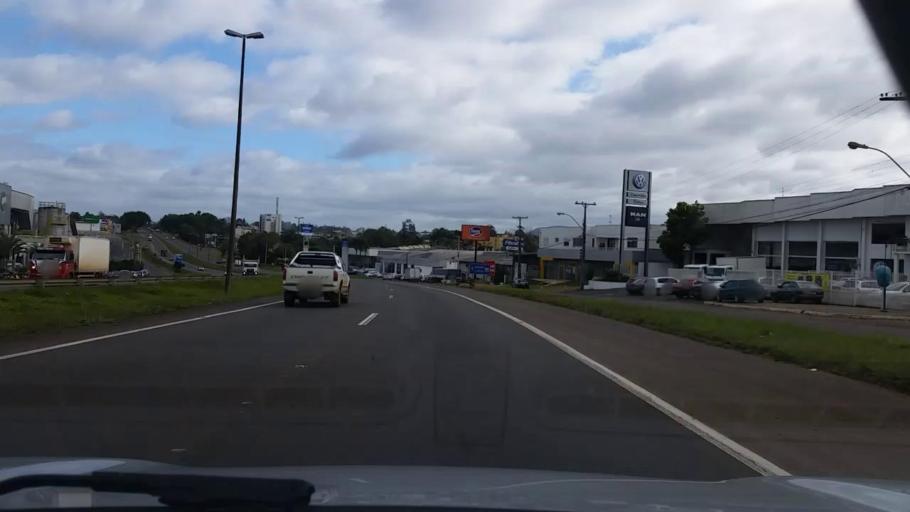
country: BR
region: Rio Grande do Sul
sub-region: Lajeado
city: Lajeado
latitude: -29.4559
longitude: -51.9579
